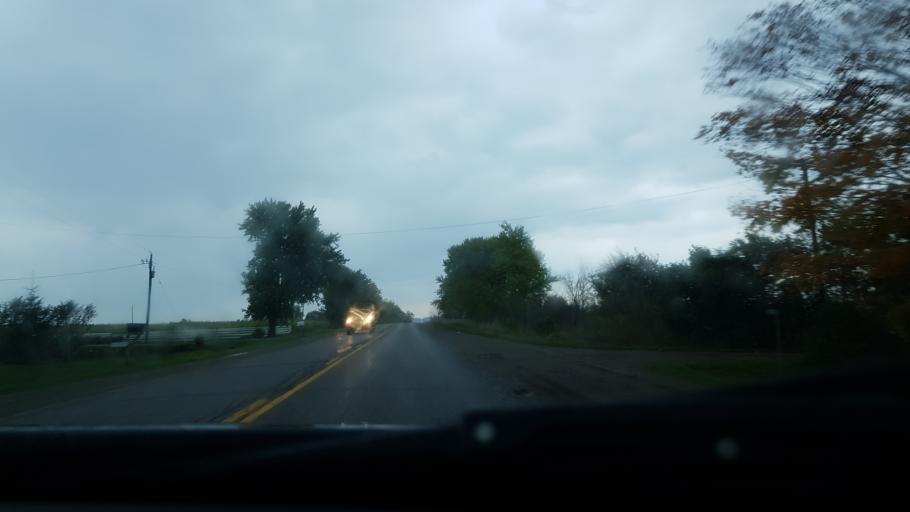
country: CA
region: Ontario
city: Omemee
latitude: 44.3822
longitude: -78.6087
